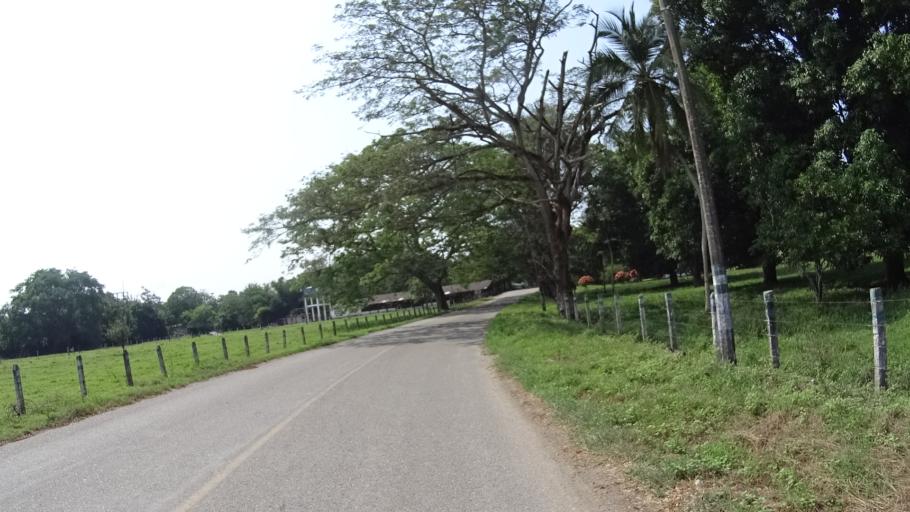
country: CO
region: Cundinamarca
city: Puerto Salgar
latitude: 5.4996
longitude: -74.6869
